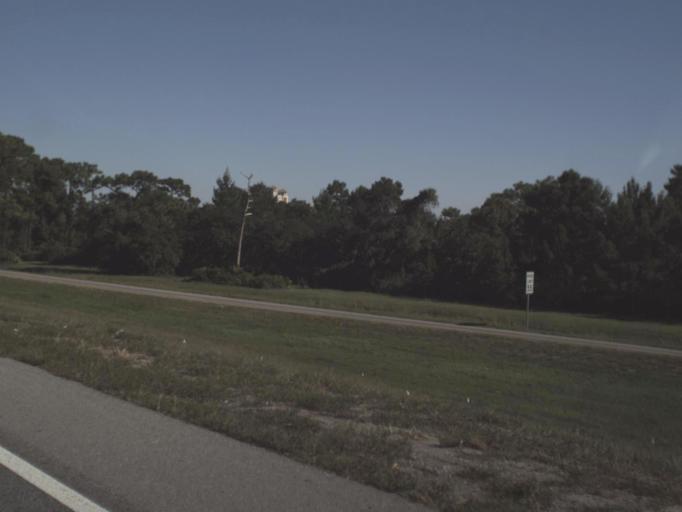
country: US
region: Florida
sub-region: Orange County
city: Williamsburg
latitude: 28.4201
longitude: -81.4726
